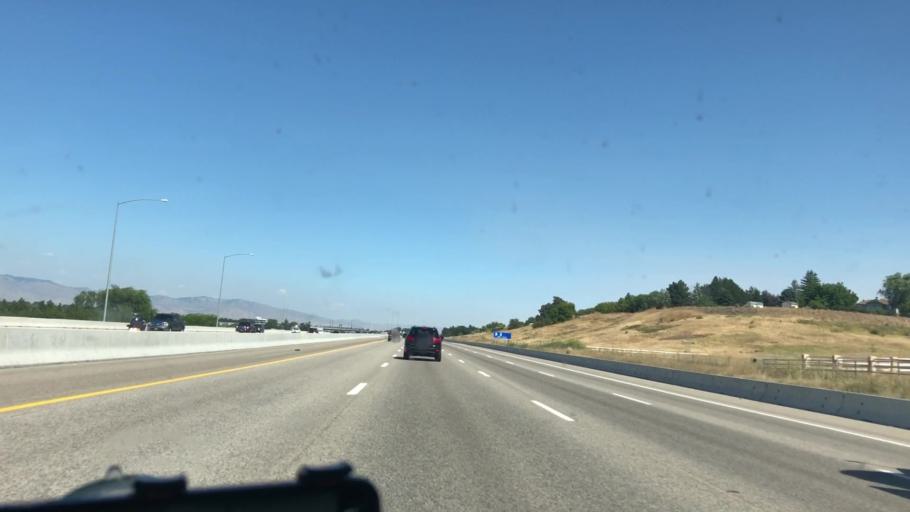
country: US
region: Idaho
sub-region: Ada County
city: Meridian
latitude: 43.5943
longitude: -116.4504
